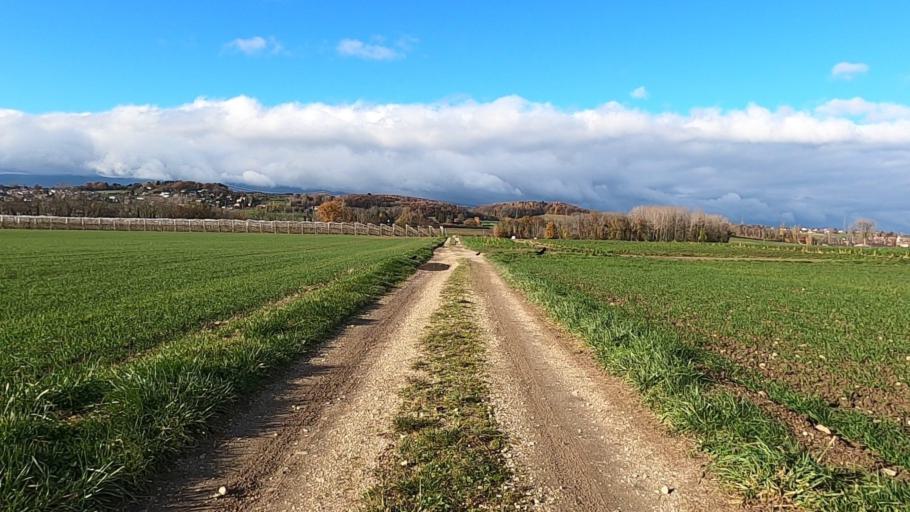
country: CH
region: Vaud
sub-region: Morges District
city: Apples
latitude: 46.5170
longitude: 6.4416
